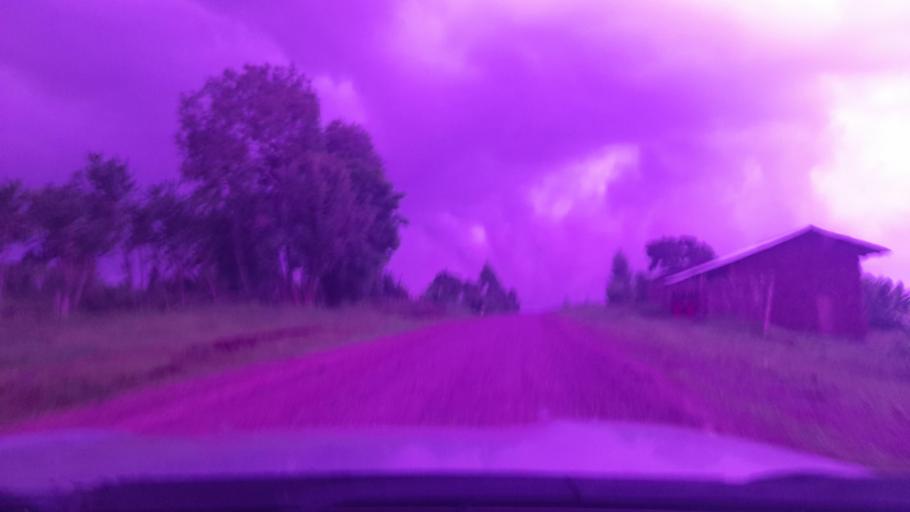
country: ET
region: Southern Nations, Nationalities, and People's Region
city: Mizan Teferi
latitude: 6.9030
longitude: 35.8395
